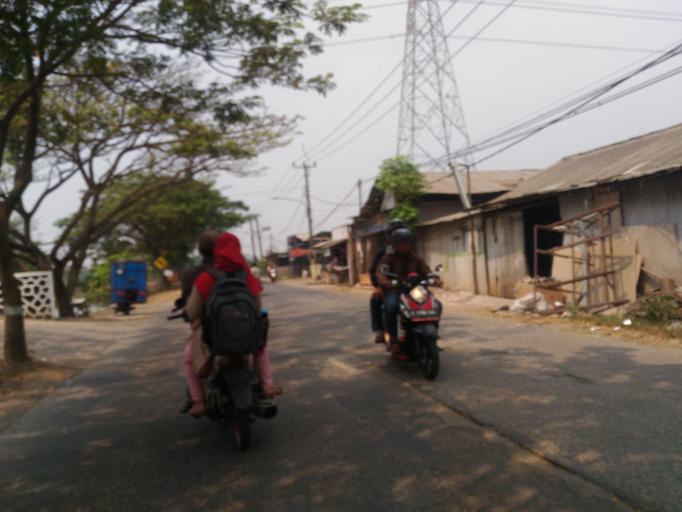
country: ID
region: West Java
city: Pasarkemis
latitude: -6.1464
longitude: 106.5542
